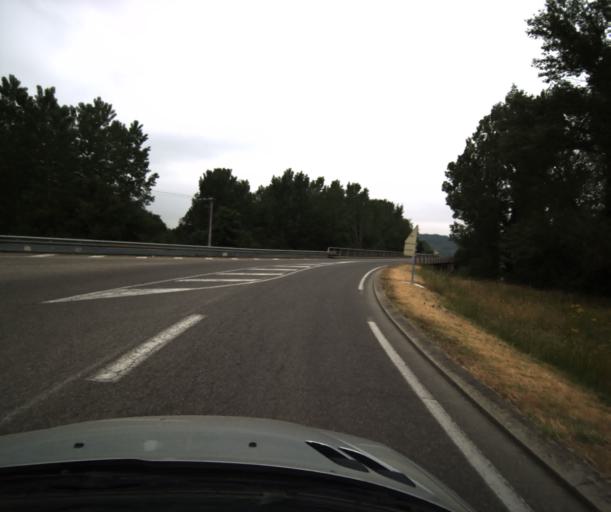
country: FR
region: Midi-Pyrenees
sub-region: Departement du Tarn-et-Garonne
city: Saint-Nicolas-de-la-Grave
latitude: 44.0756
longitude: 0.9955
